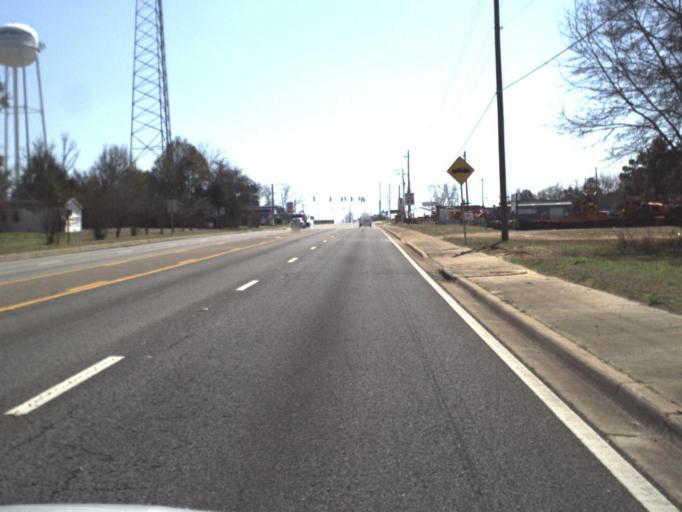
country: US
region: Florida
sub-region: Jackson County
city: Graceville
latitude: 30.9525
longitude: -85.4025
